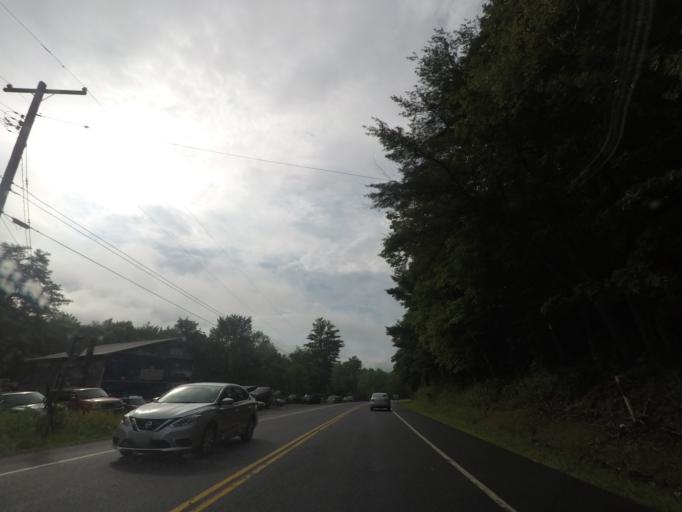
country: US
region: New York
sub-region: Rensselaer County
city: Nassau
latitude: 42.5085
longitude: -73.5635
